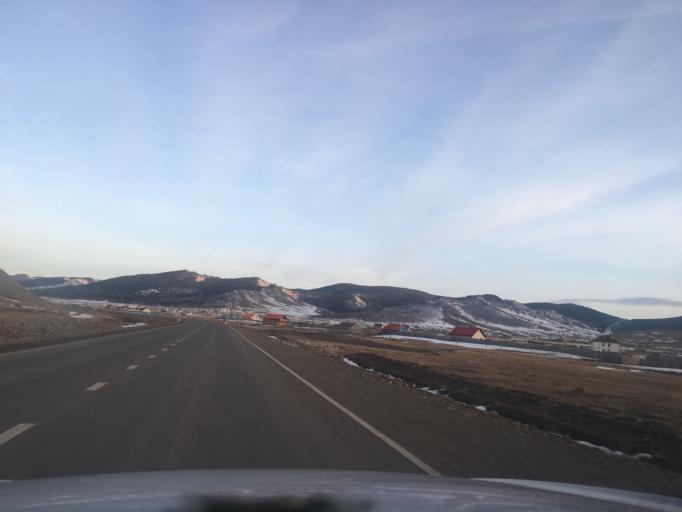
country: MN
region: Ulaanbaatar
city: Ulaanbaatar
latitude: 48.0969
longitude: 106.7414
